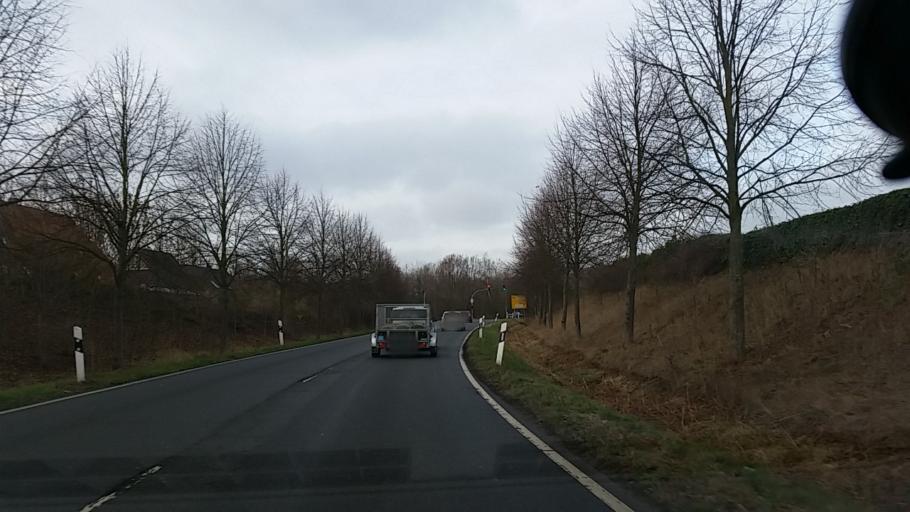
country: DE
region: Lower Saxony
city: Wolfsburg
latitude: 52.4498
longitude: 10.8318
